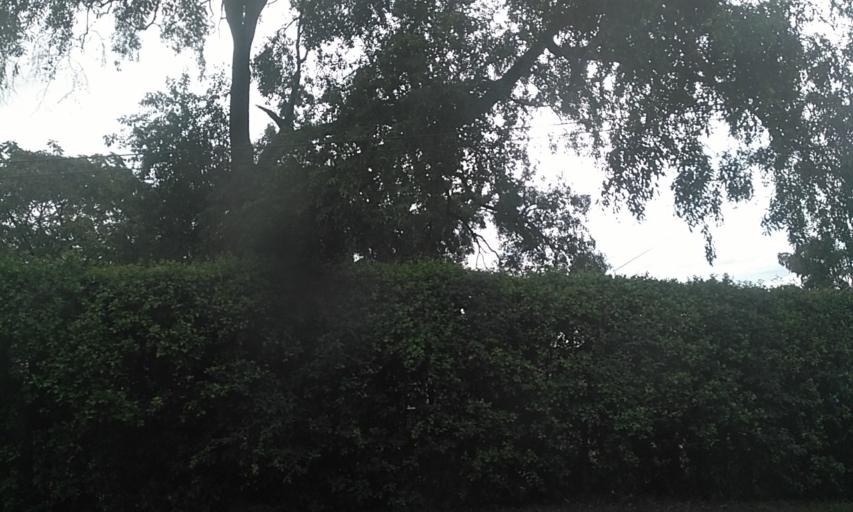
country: UG
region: Central Region
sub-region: Kampala District
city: Kampala
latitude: 0.3287
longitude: 32.5959
